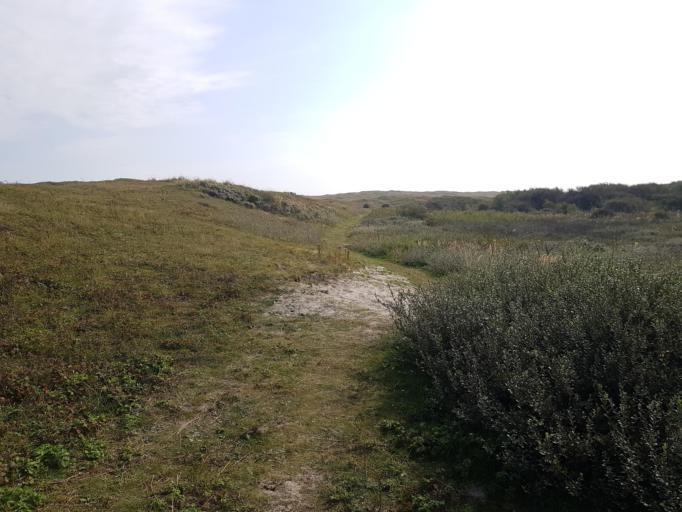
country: NL
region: North Holland
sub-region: Gemeente Texel
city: Den Burg
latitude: 53.1744
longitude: 4.8403
